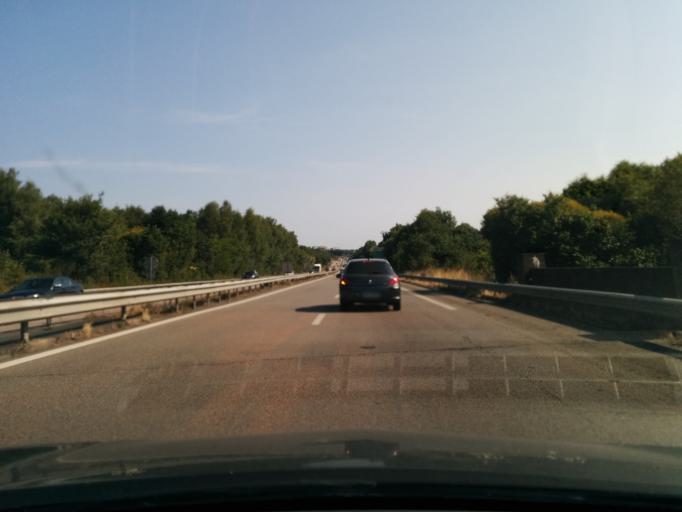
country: FR
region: Limousin
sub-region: Departement de la Haute-Vienne
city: Rilhac-Rancon
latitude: 45.9063
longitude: 1.2916
